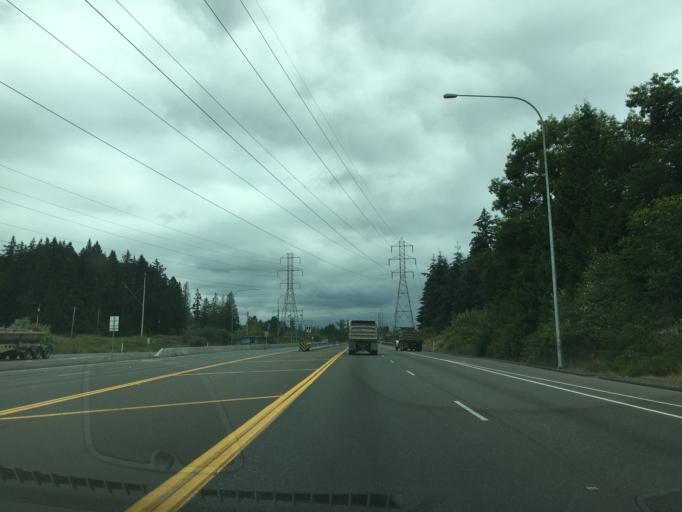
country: US
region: Washington
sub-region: Snohomish County
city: West Lake Stevens
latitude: 48.0221
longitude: -122.1093
